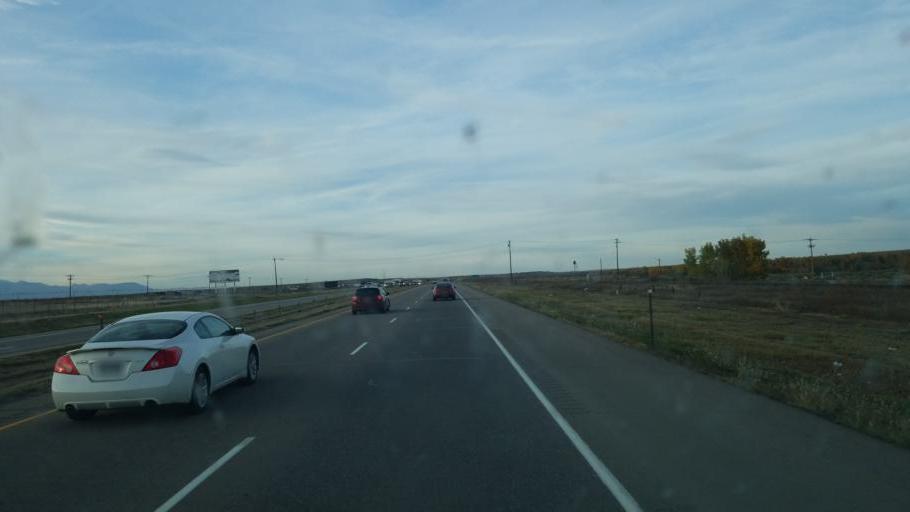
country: US
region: Colorado
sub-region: Pueblo County
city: Pueblo
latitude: 38.3528
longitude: -104.6203
